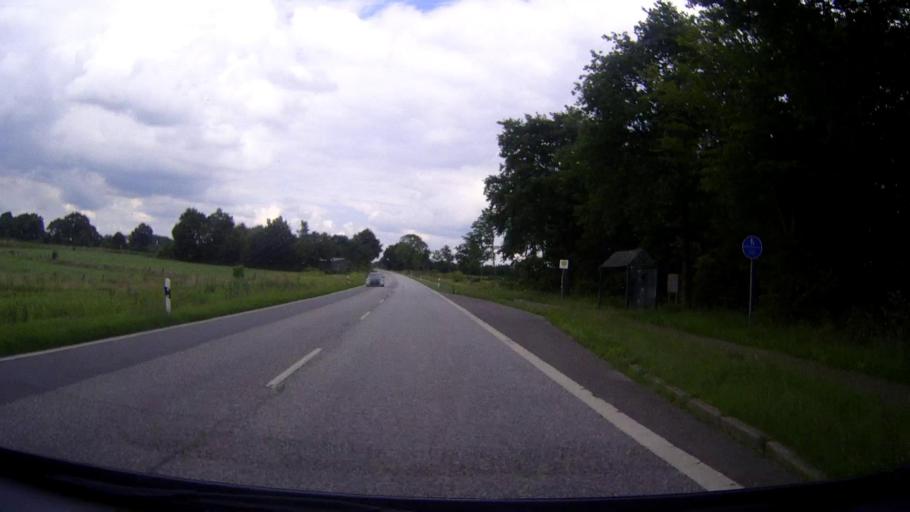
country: DE
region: Schleswig-Holstein
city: Beldorf
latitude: 54.1227
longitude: 9.3762
